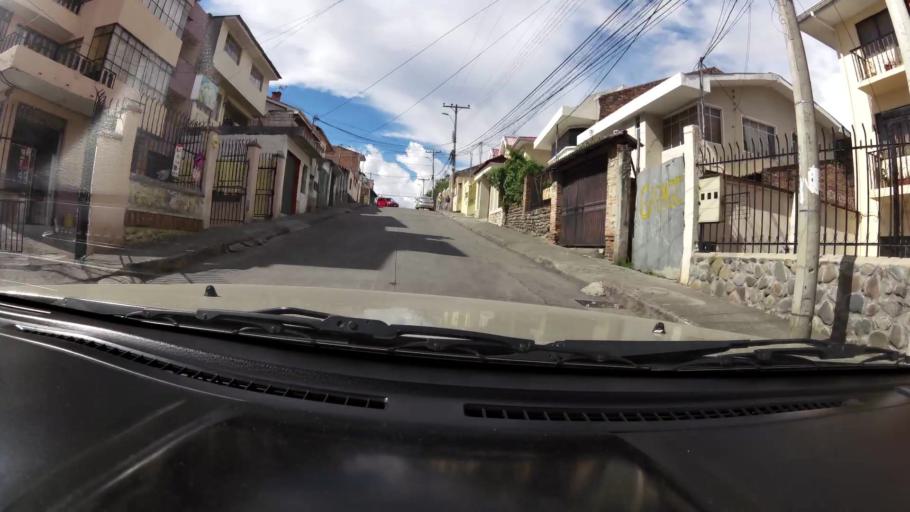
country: EC
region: Azuay
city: Cuenca
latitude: -2.8865
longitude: -79.0007
